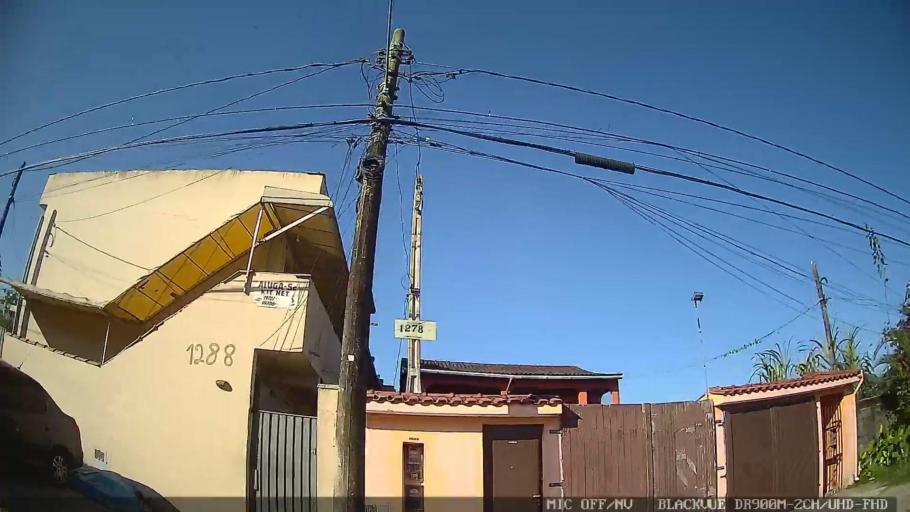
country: BR
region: Sao Paulo
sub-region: Guaruja
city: Guaruja
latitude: -23.9739
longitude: -46.2240
